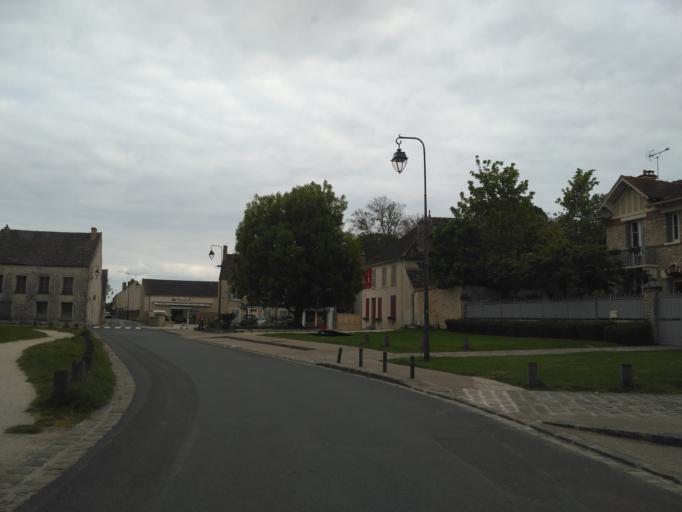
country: FR
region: Ile-de-France
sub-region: Departement de Seine-et-Marne
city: Moisenay
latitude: 48.5667
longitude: 2.7809
